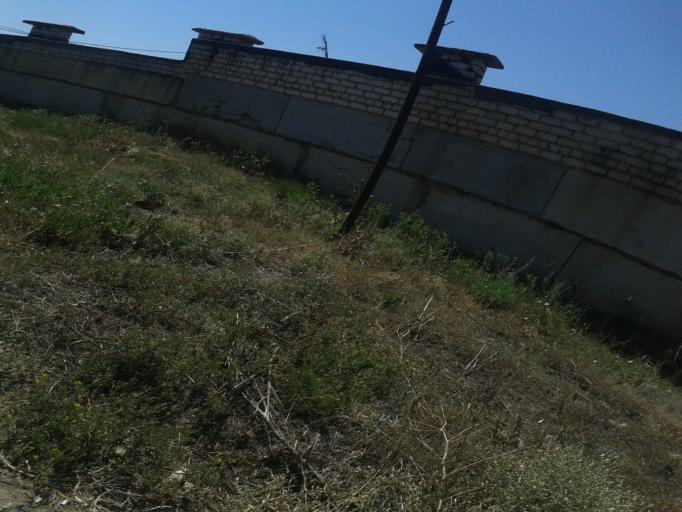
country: RU
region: Volgograd
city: Volgograd
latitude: 48.6888
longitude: 44.4513
